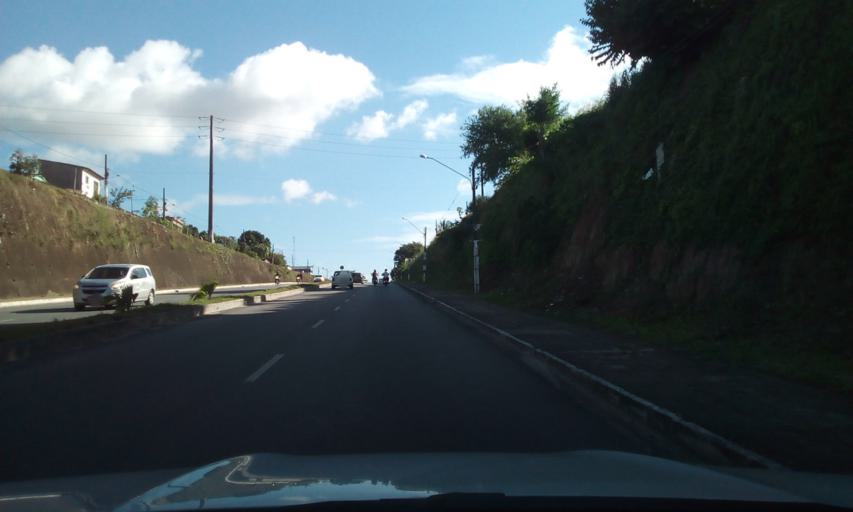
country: BR
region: Paraiba
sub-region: Bayeux
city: Bayeux
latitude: -7.1336
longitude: -34.9355
